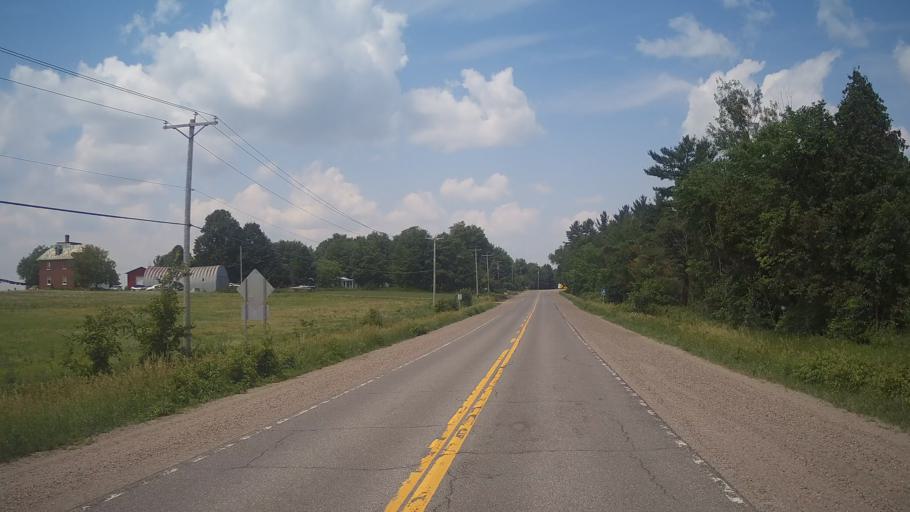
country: CA
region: Quebec
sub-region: Outaouais
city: Shawville
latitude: 45.5731
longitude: -76.4422
